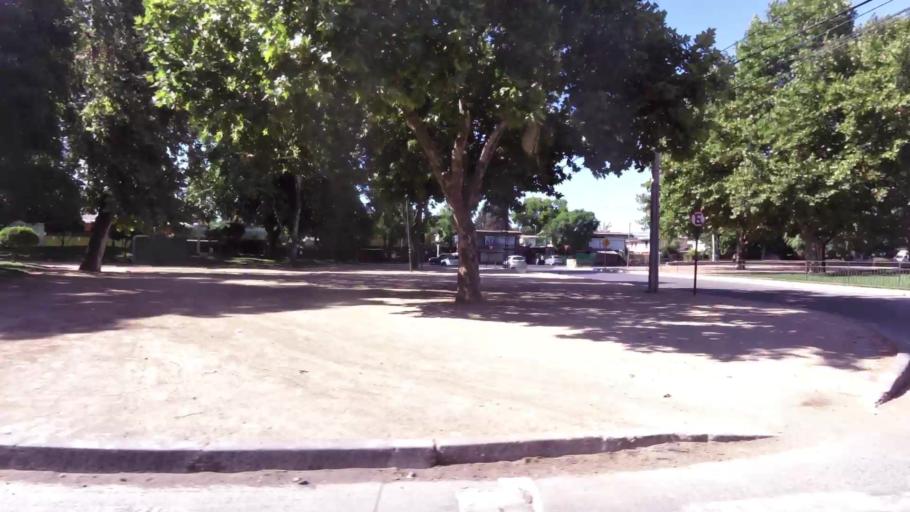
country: CL
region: Maule
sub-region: Provincia de Talca
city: Talca
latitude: -35.4232
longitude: -71.6514
